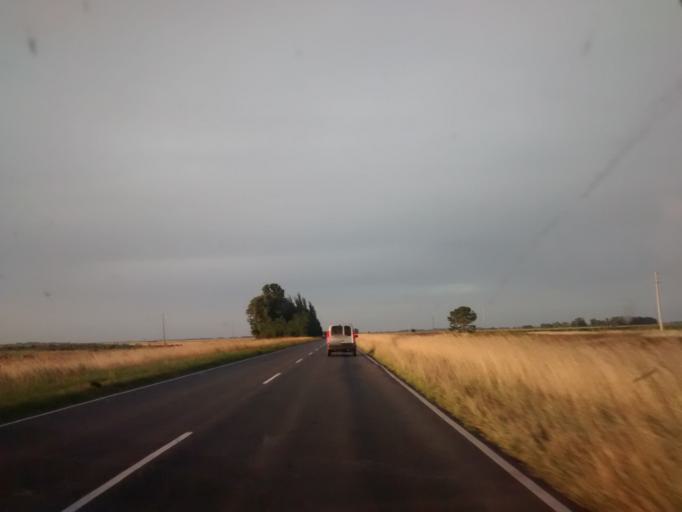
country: AR
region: Buenos Aires
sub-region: Partido de General Belgrano
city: General Belgrano
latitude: -35.9546
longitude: -58.6207
